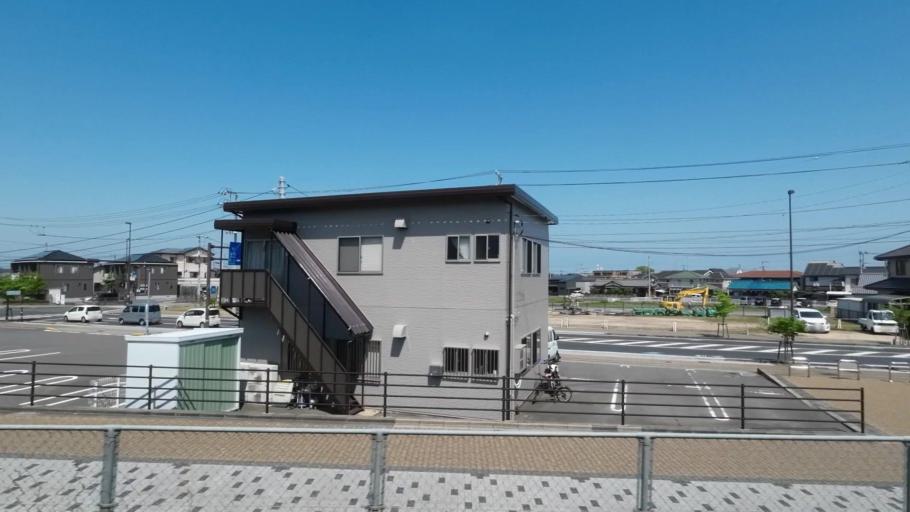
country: JP
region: Ehime
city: Niihama
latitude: 33.9509
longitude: 133.2978
